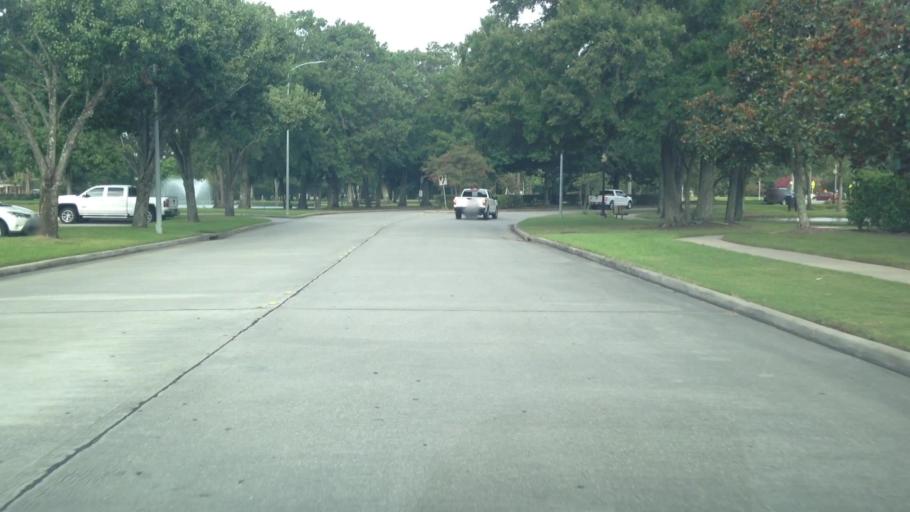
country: US
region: Texas
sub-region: Harris County
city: Atascocita
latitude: 29.9263
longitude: -95.1781
